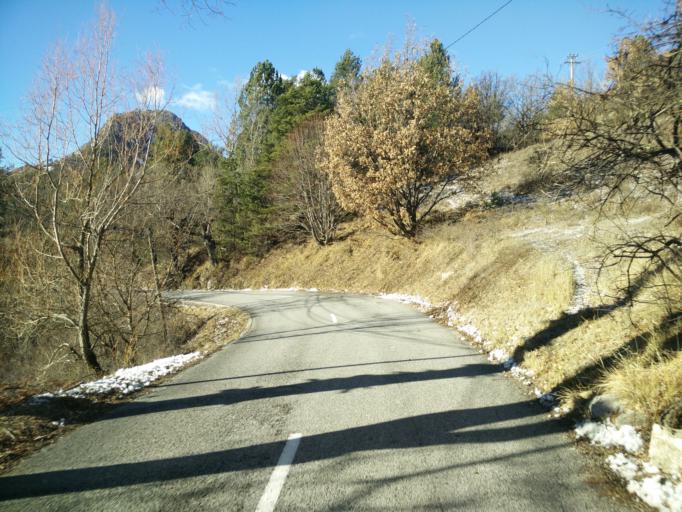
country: FR
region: Provence-Alpes-Cote d'Azur
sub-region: Departement des Alpes-de-Haute-Provence
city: Castellane
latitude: 43.8291
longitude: 6.4669
